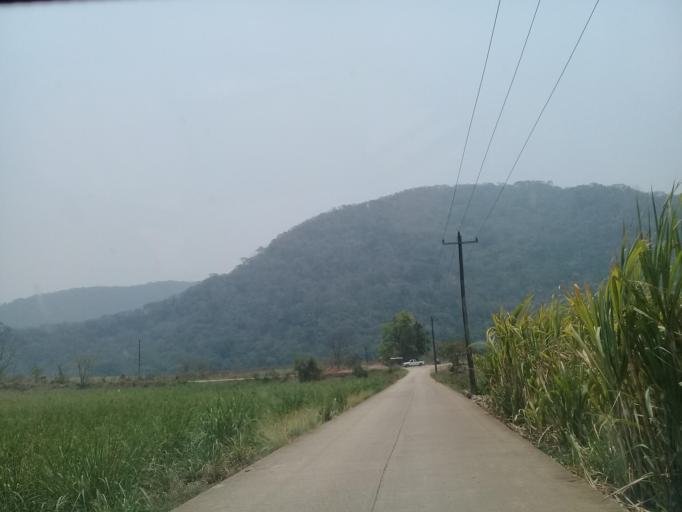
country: MX
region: Veracruz
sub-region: Tezonapa
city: Laguna Chica (Pueblo Nuevo)
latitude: 18.5685
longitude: -96.7216
